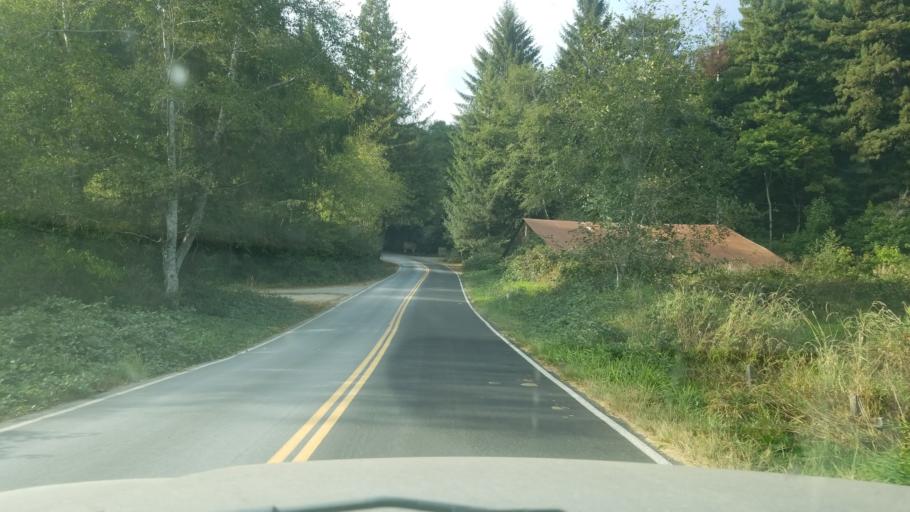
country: US
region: California
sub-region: Humboldt County
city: Westhaven-Moonstone
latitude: 41.3231
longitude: -124.0432
